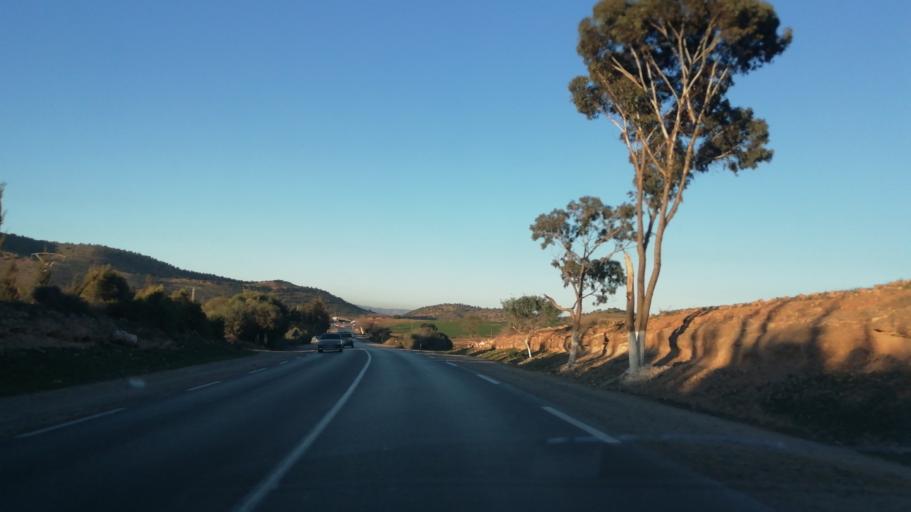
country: DZ
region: Tlemcen
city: Nedroma
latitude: 34.8576
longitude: -1.6790
